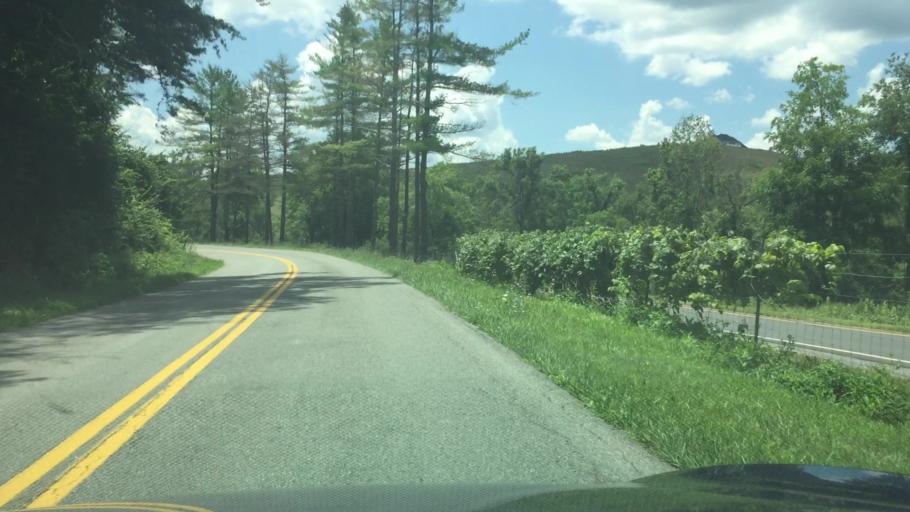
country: US
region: Virginia
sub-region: Pulaski County
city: Pulaski
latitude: 36.9927
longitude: -80.7914
